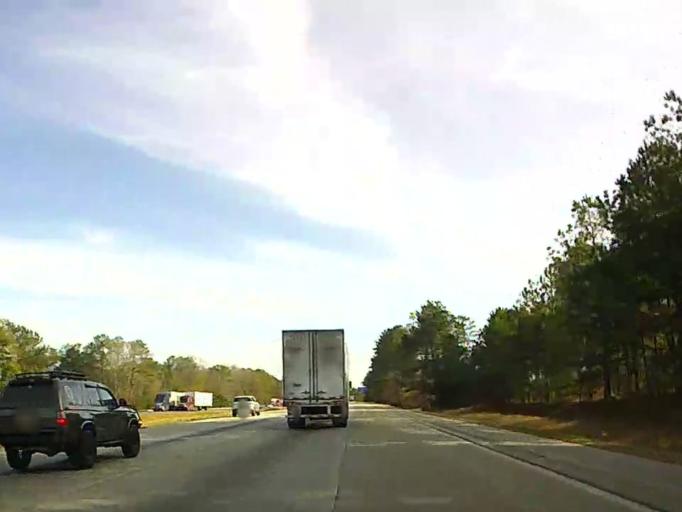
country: US
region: Georgia
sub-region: Monroe County
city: Forsyth
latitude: 32.9874
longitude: -83.8390
